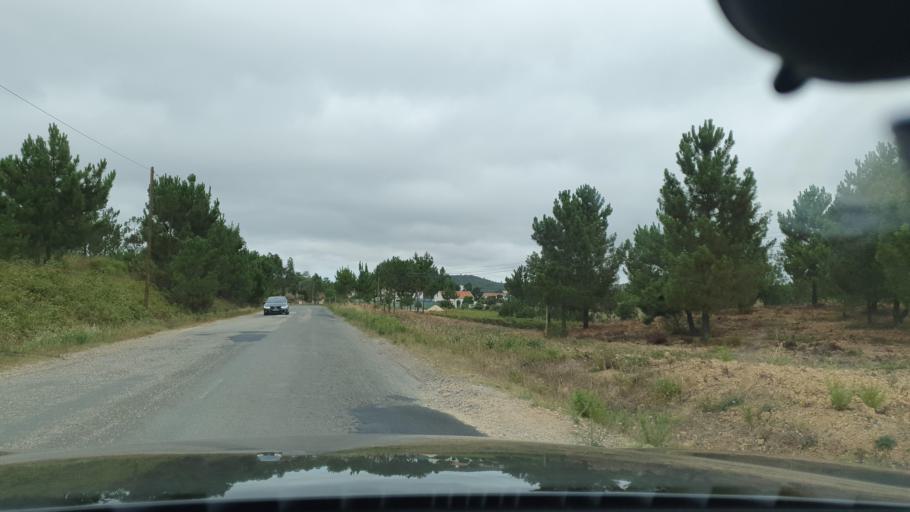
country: PT
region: Beja
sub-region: Odemira
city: Sao Teotonio
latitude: 37.5037
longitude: -8.6904
